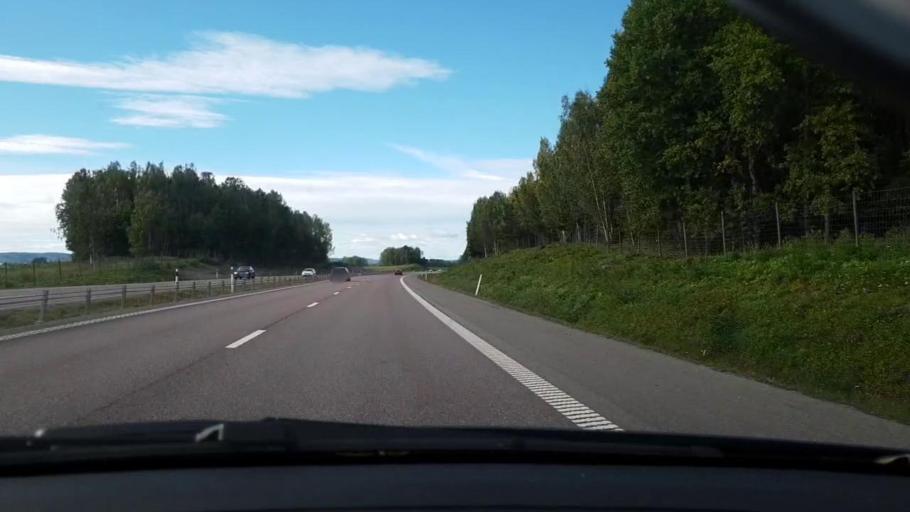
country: SE
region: Dalarna
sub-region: Borlange Kommun
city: Ornas
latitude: 60.4971
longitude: 15.5079
